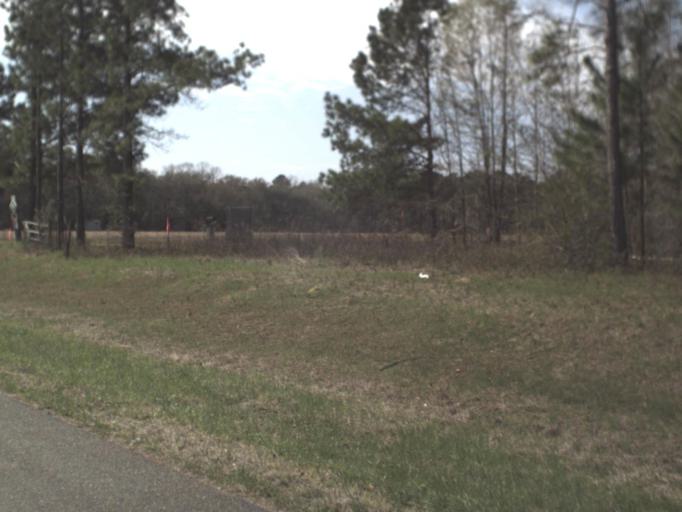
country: US
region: Florida
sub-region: Gadsden County
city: Gretna
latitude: 30.5502
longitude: -84.7575
